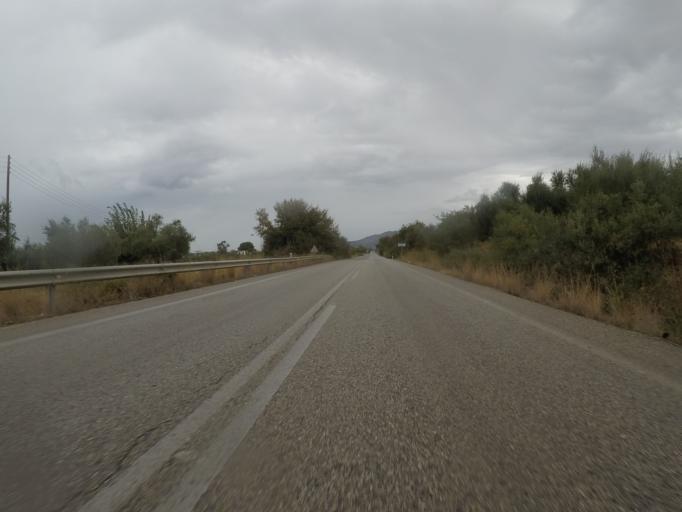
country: GR
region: West Greece
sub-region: Nomos Ileias
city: Zacharo
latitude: 37.4252
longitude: 21.6674
